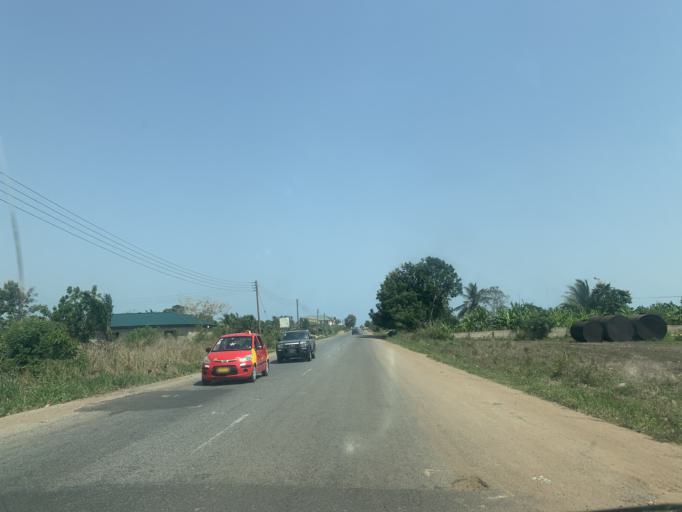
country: GH
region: Central
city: Winneba
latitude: 5.4025
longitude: -0.6517
